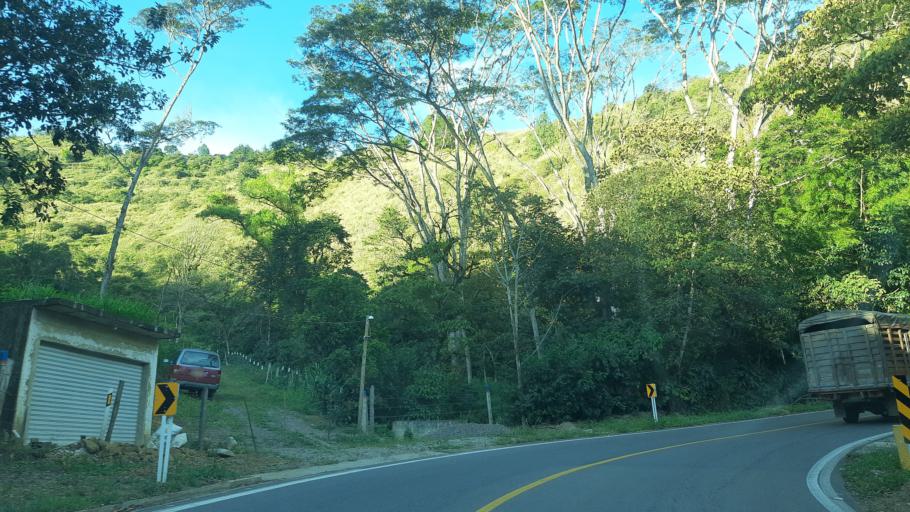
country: CO
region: Boyaca
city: Guateque
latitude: 5.0069
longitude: -73.4990
